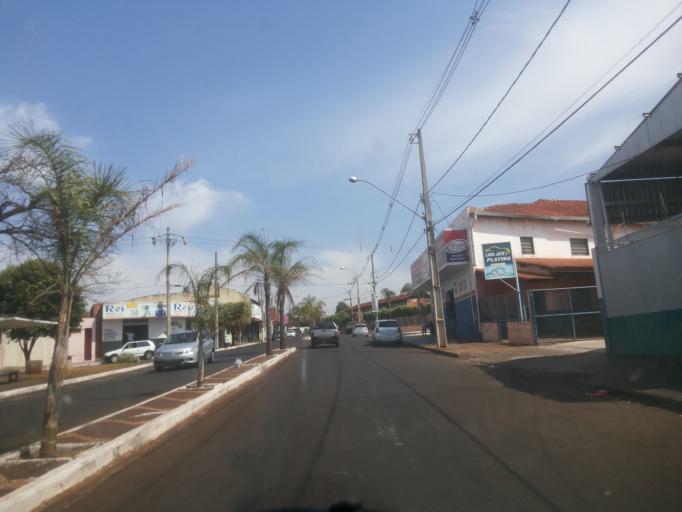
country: BR
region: Minas Gerais
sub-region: Ituiutaba
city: Ituiutaba
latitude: -18.9774
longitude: -49.4748
